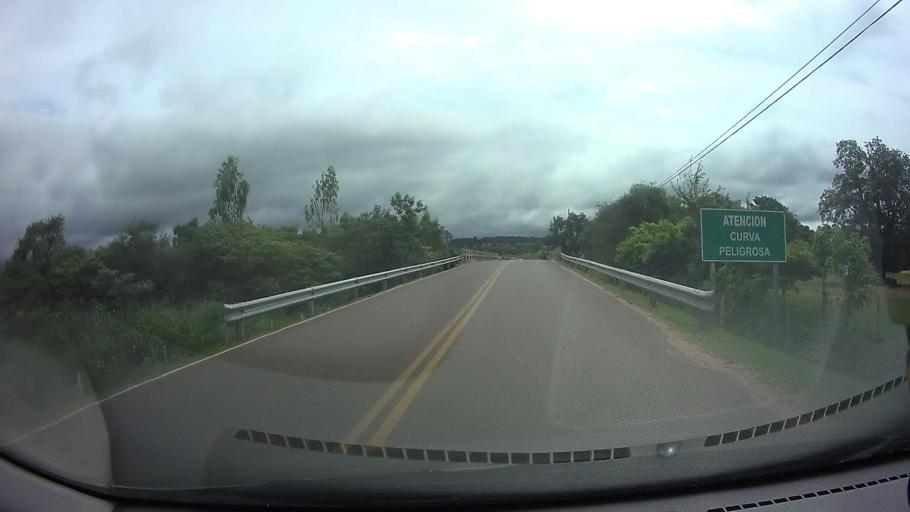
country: PY
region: Cordillera
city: Atyra
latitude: -25.2794
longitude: -57.1814
